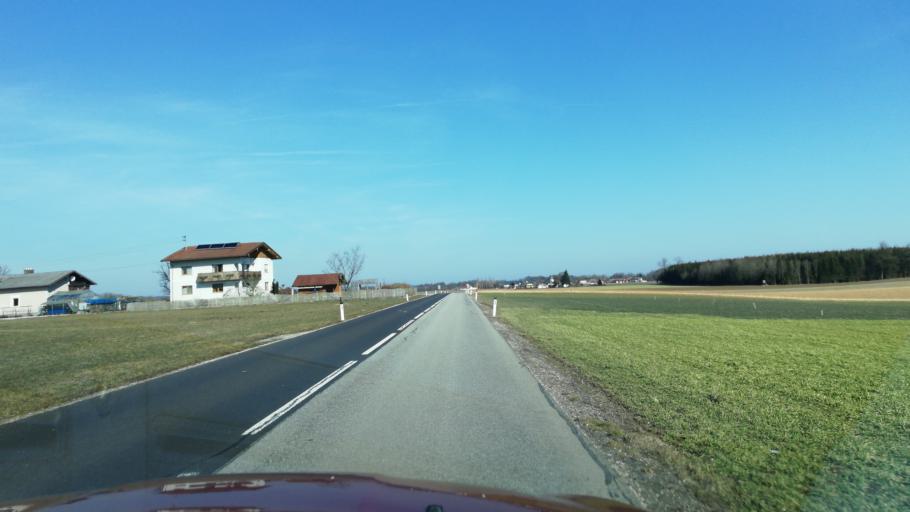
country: AT
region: Upper Austria
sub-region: Politischer Bezirk Vocklabruck
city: Desselbrunn
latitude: 48.0107
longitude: 13.7558
